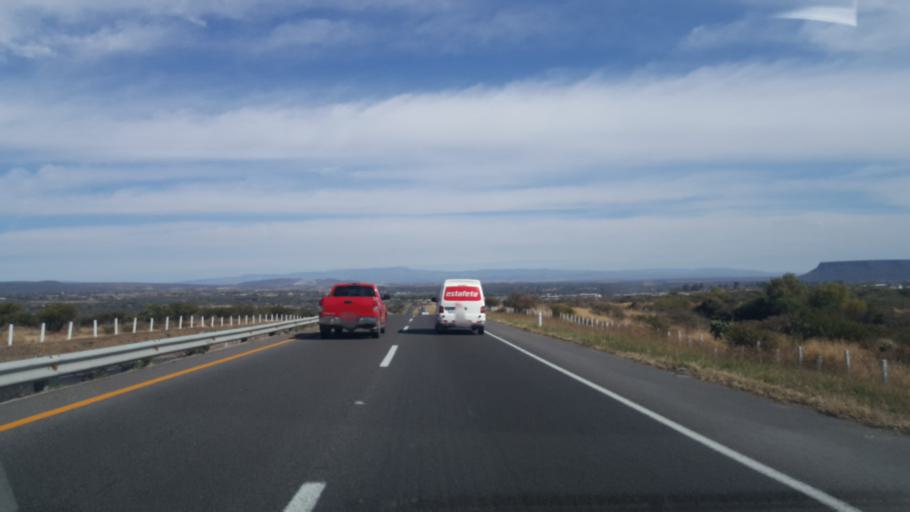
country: MX
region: Jalisco
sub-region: Lagos de Moreno
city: Cristeros [Fraccionamiento]
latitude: 21.3085
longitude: -102.0737
